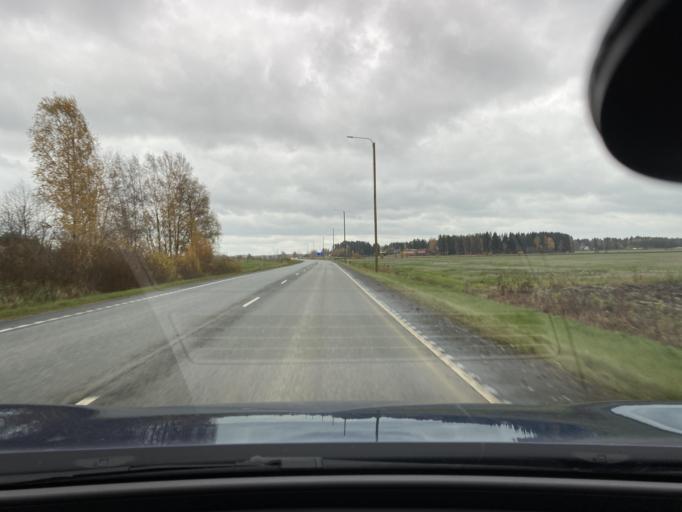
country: FI
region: Satakunta
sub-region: Rauma
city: Eura
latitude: 61.1608
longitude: 22.0875
